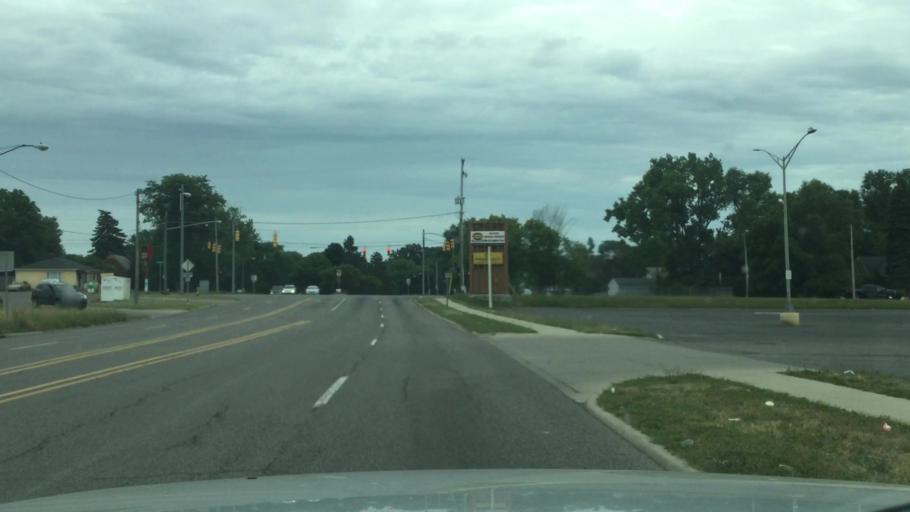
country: US
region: Michigan
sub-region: Genesee County
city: Beecher
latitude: 43.0620
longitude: -83.7049
